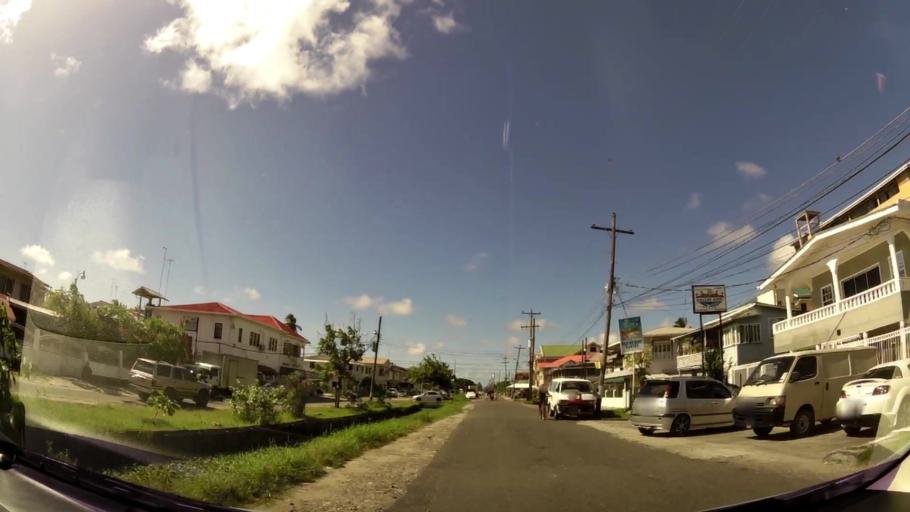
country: GY
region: Demerara-Mahaica
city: Georgetown
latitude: 6.8125
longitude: -58.1405
